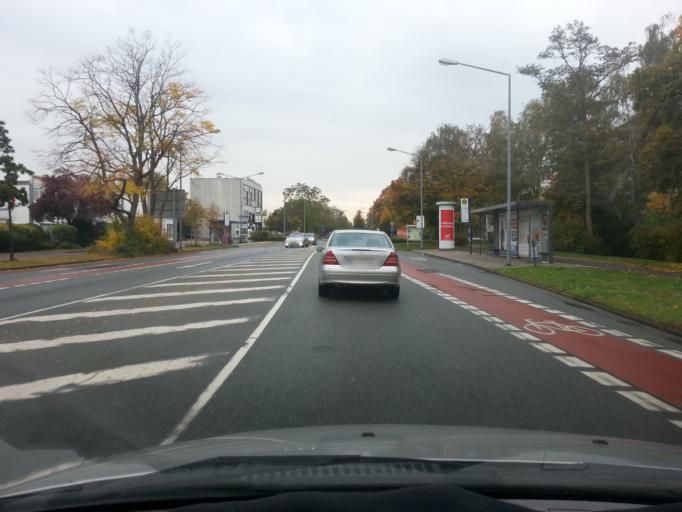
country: DE
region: Hesse
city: Dreieich
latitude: 50.0336
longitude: 8.6953
